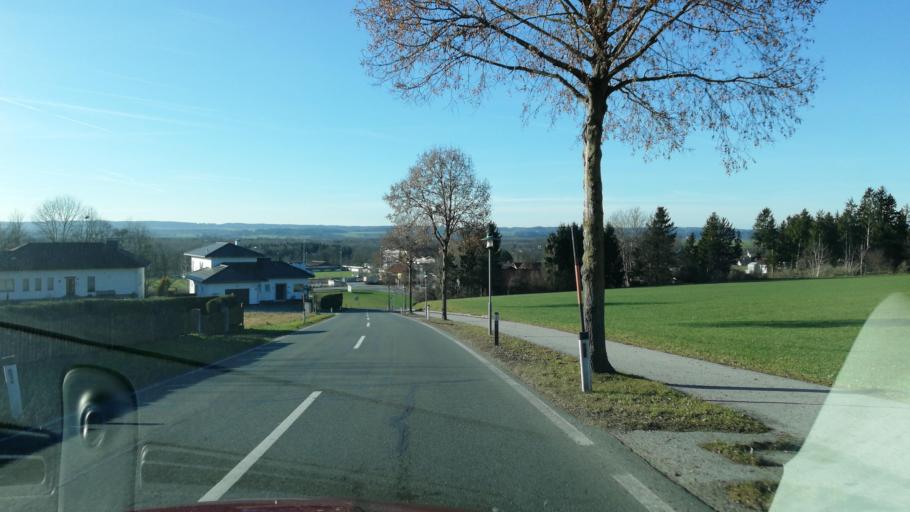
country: DE
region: Bavaria
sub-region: Upper Bavaria
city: Fridolfing
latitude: 48.0412
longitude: 12.8370
